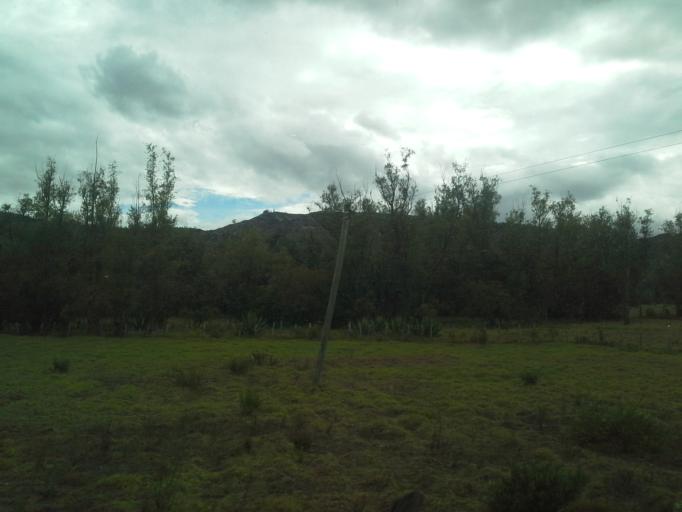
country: CO
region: Boyaca
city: Raquira
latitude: 5.5583
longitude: -73.6443
